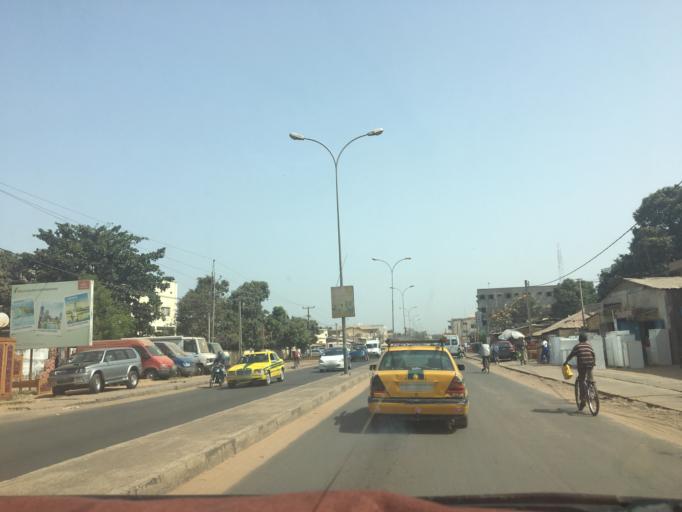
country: GM
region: Western
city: Abuko
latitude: 13.4338
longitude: -16.6758
